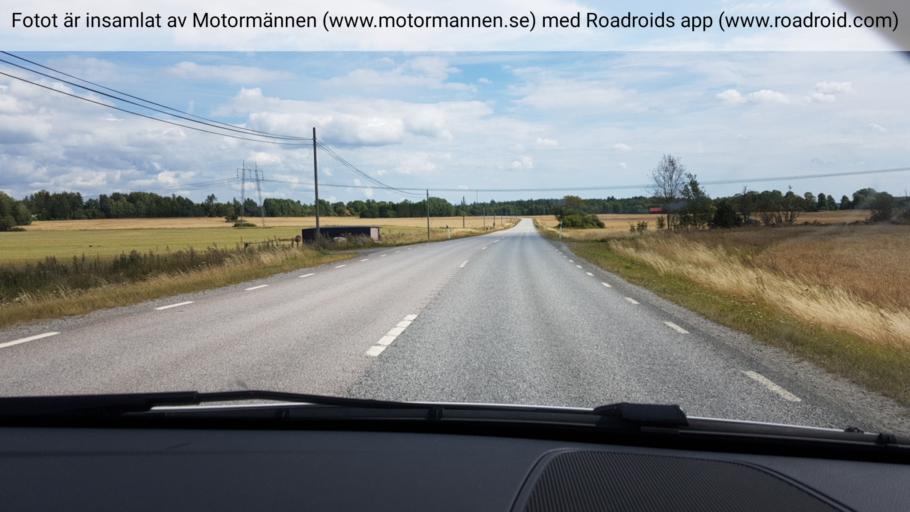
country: SE
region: Stockholm
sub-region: Vallentuna Kommun
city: Vallentuna
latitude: 59.6540
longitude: 18.0290
